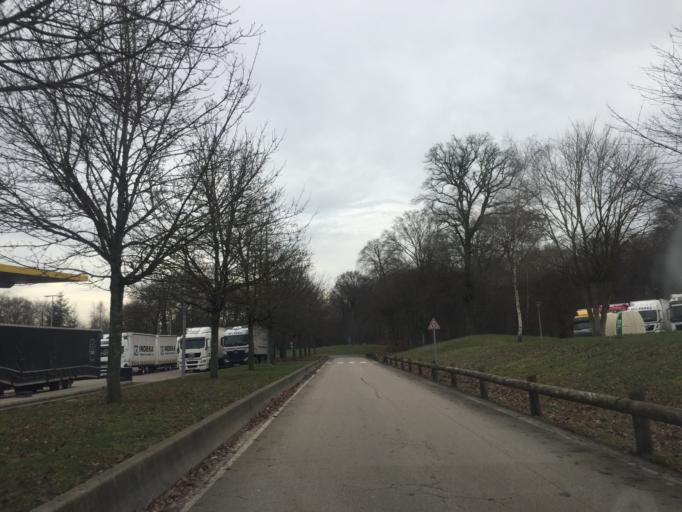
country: FR
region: Franche-Comte
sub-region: Departement du Jura
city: Bletterans
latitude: 46.7751
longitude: 5.5231
